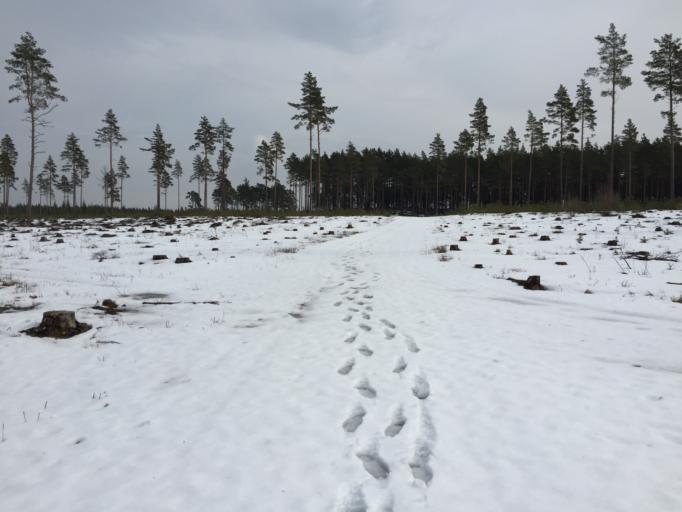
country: EE
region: Saare
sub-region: Kuressaare linn
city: Kuressaare
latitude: 58.3955
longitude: 22.1652
